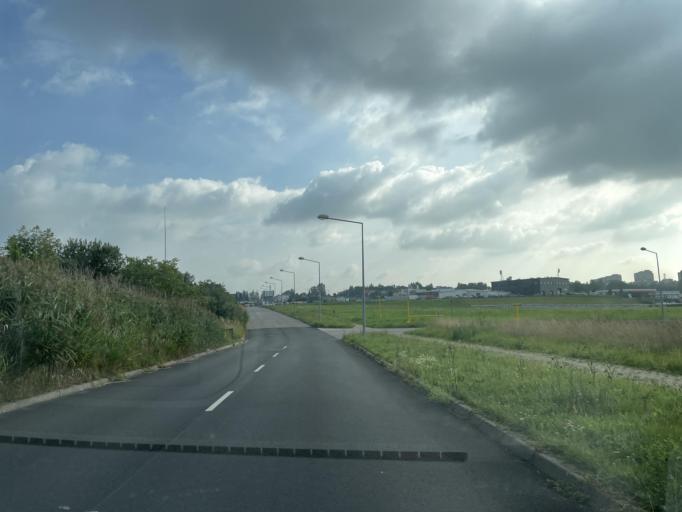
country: PL
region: Silesian Voivodeship
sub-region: Powiat bedzinski
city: Bedzin
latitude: 50.3034
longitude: 19.1704
